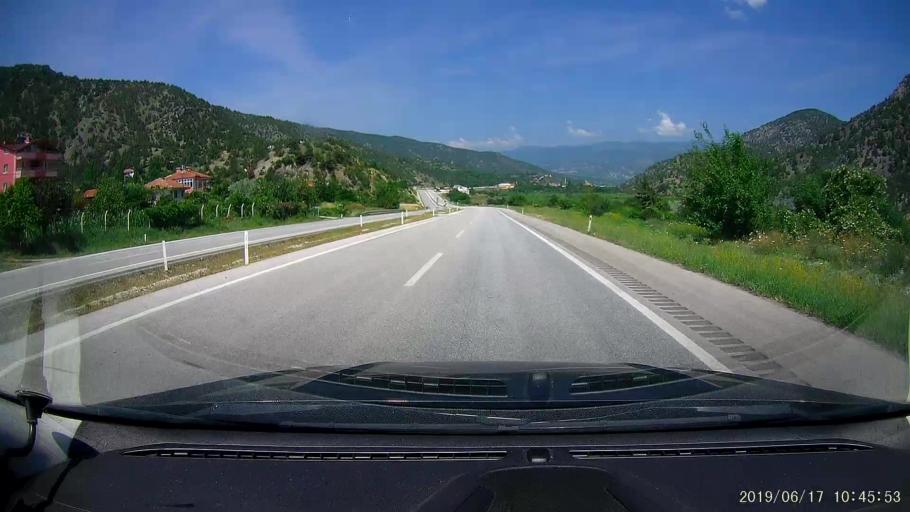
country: TR
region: Corum
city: Hacihamza
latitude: 41.0640
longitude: 34.4764
